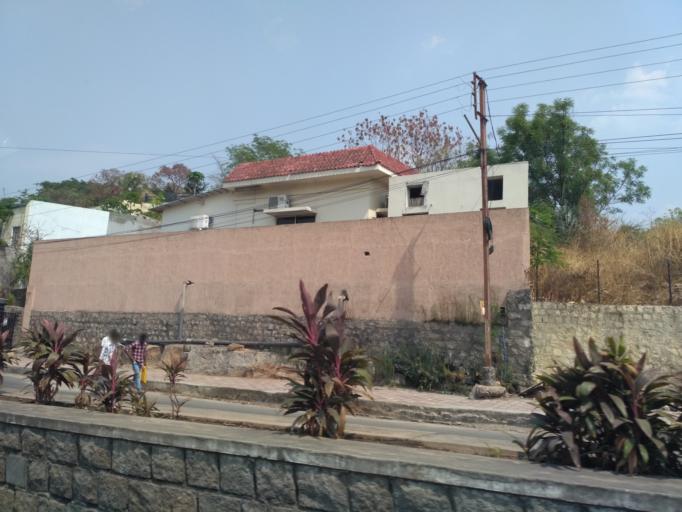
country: IN
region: Telangana
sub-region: Rangareddi
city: Kukatpalli
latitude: 17.4337
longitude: 78.4084
